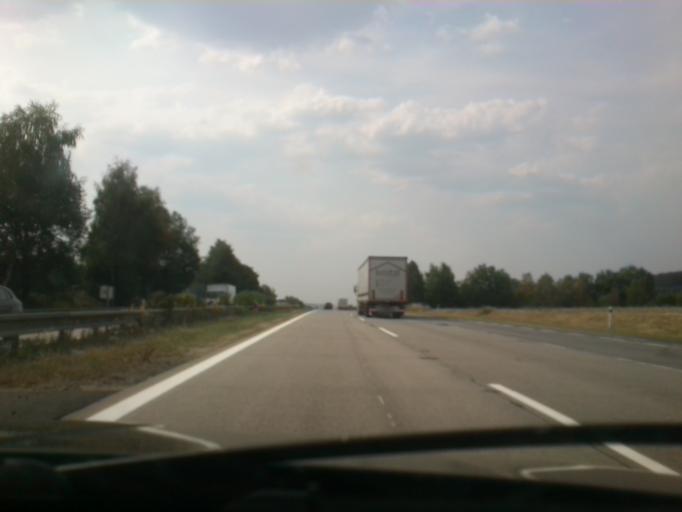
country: CZ
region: Central Bohemia
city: Divisov
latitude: 49.8021
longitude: 14.9065
